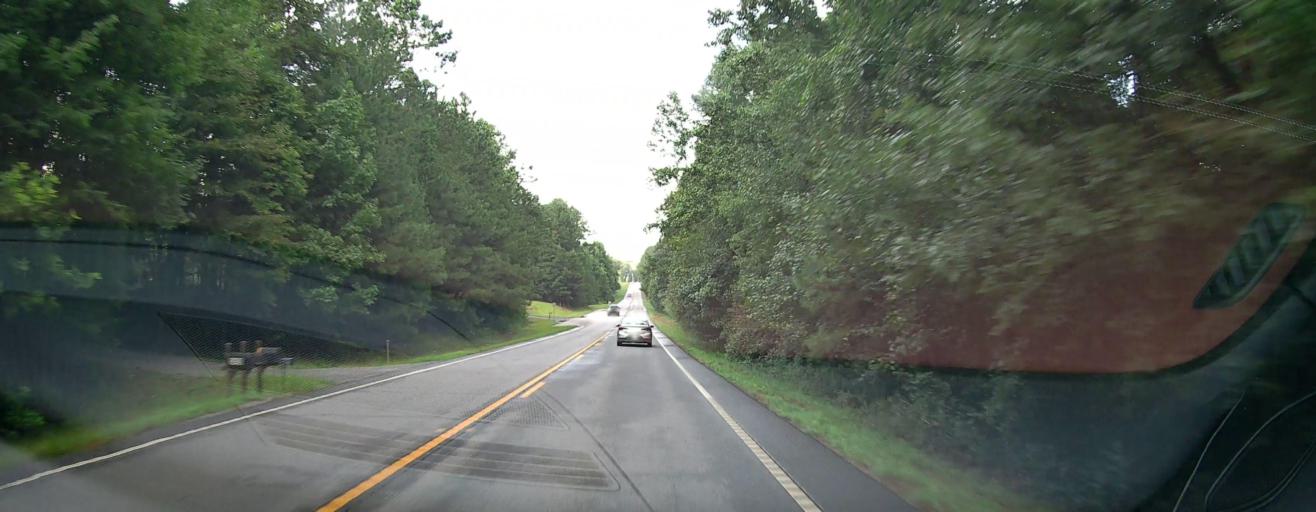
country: US
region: Georgia
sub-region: Coweta County
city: Senoia
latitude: 33.2816
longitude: -84.5503
